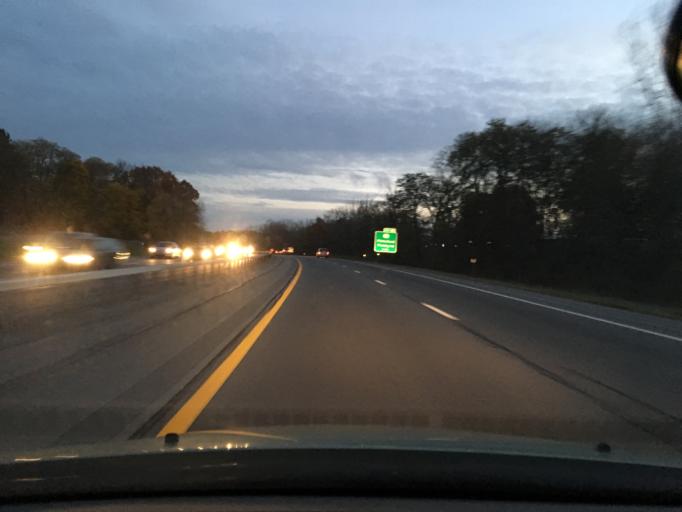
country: US
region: New York
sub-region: Monroe County
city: Pittsford
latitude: 43.0911
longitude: -77.4998
